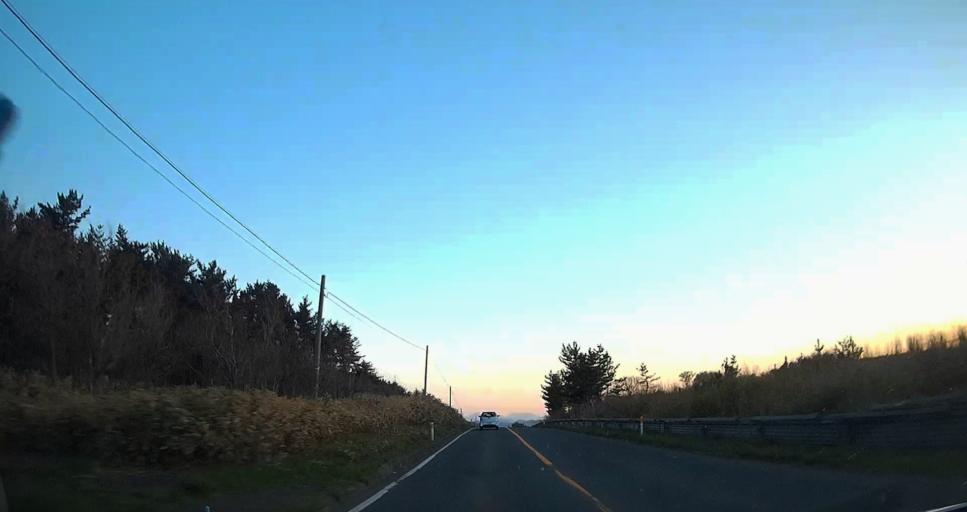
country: JP
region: Aomori
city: Misawa
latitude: 40.8917
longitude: 141.1658
